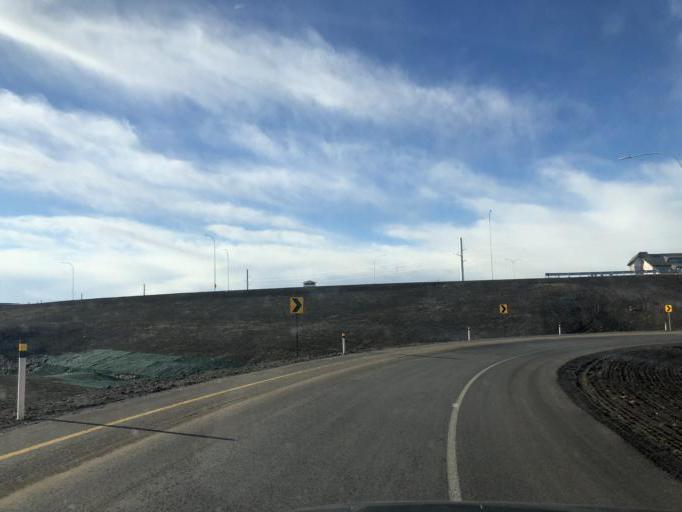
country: CA
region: Alberta
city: Calgary
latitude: 50.9490
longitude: -114.1418
